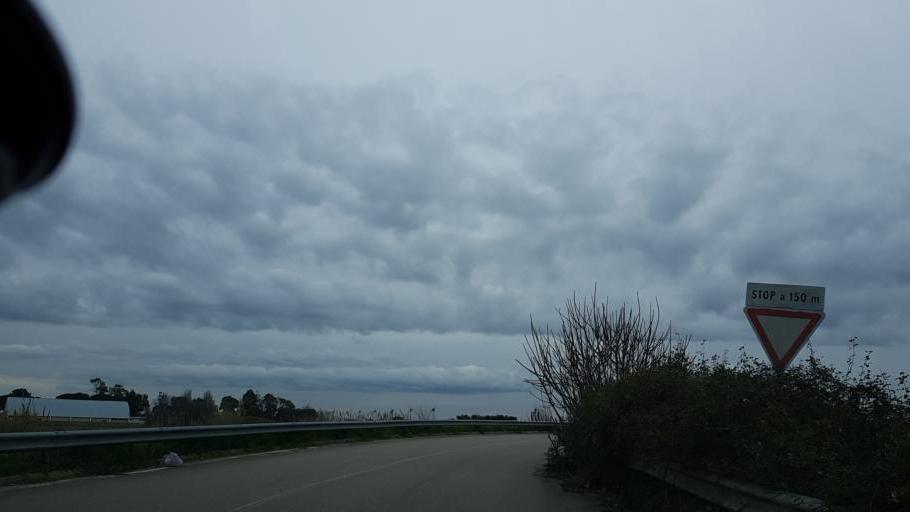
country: IT
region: Apulia
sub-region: Provincia di Brindisi
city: La Rosa
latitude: 40.6175
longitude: 17.9462
